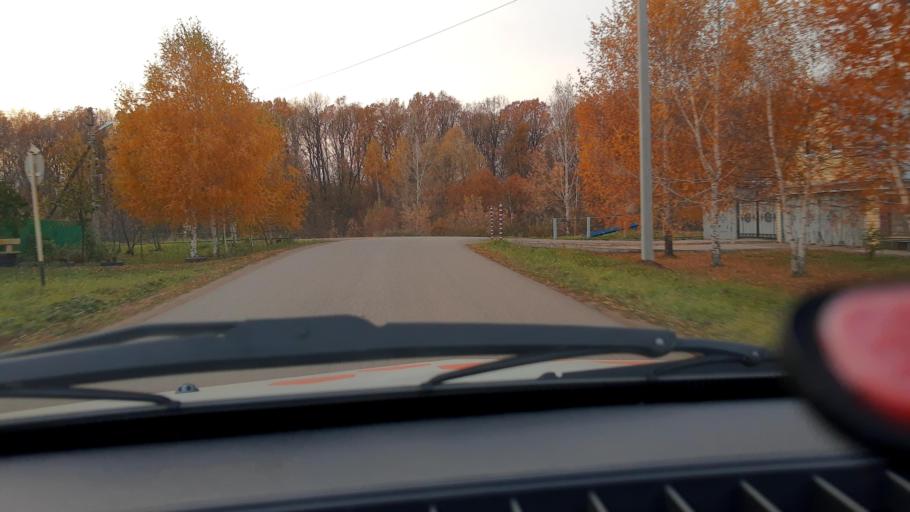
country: RU
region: Bashkortostan
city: Iglino
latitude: 54.7962
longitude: 56.3138
